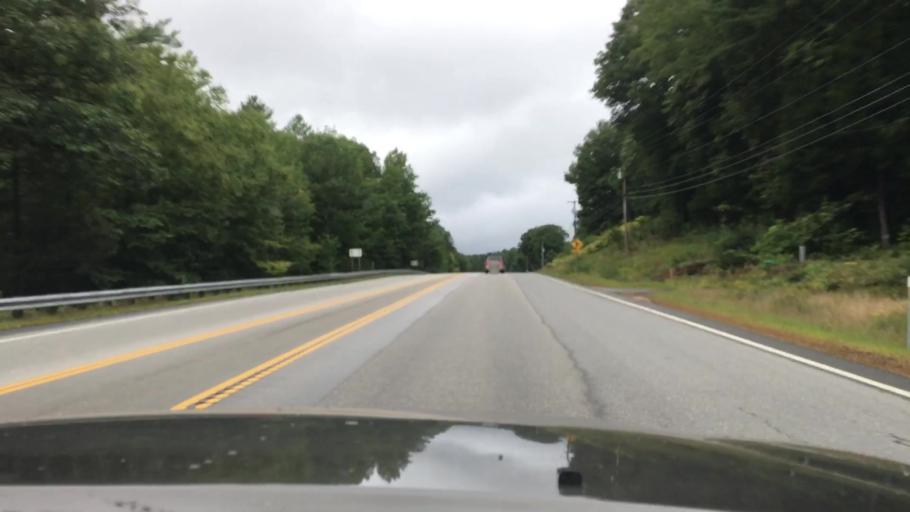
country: US
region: New Hampshire
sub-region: Cheshire County
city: Chesterfield
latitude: 42.9016
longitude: -72.4625
